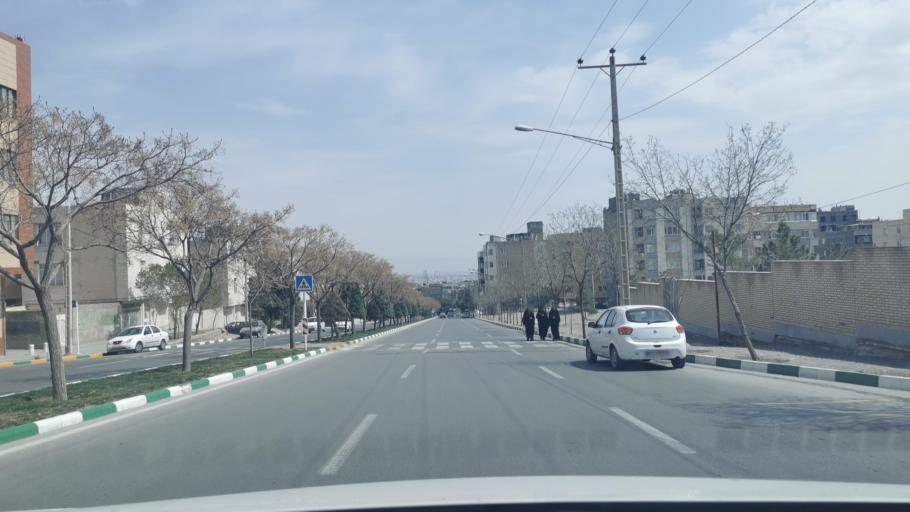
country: IR
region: Razavi Khorasan
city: Mashhad
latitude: 36.2886
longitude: 59.5003
